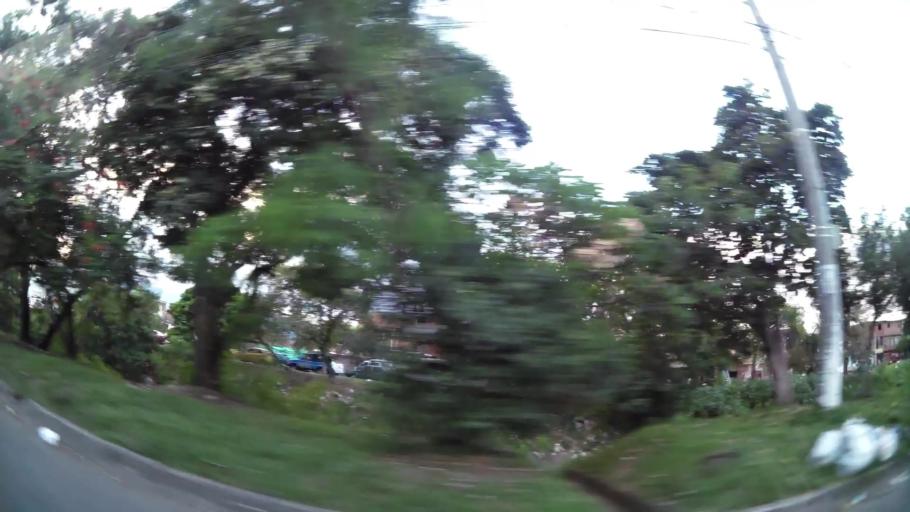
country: CO
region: Valle del Cauca
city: Cali
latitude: 3.4250
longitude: -76.4849
